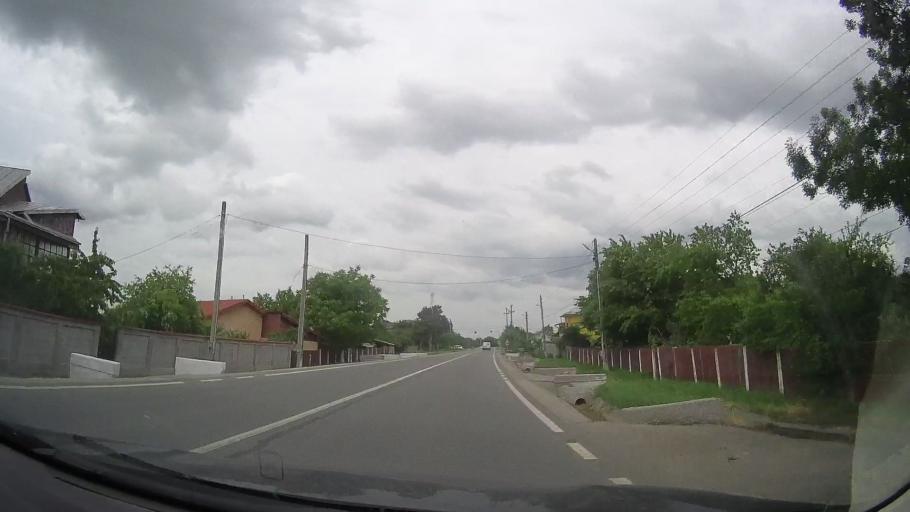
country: RO
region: Dolj
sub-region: Comuna Leu
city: Leu
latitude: 44.1891
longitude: 23.9912
